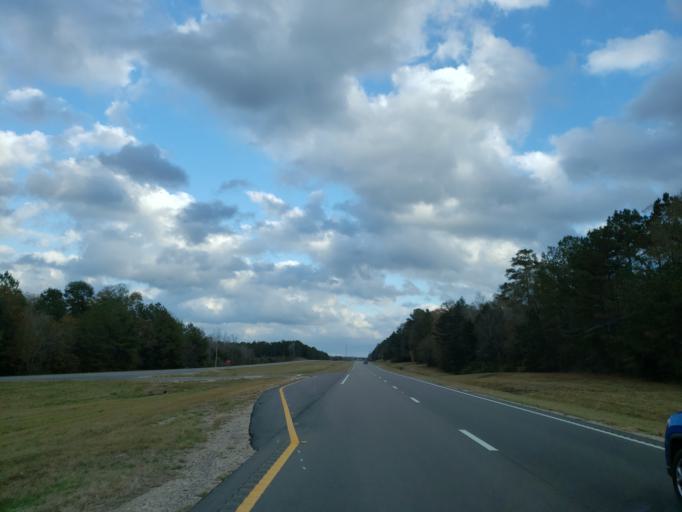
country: US
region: Mississippi
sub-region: Perry County
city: New Augusta
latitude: 31.2058
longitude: -89.0717
